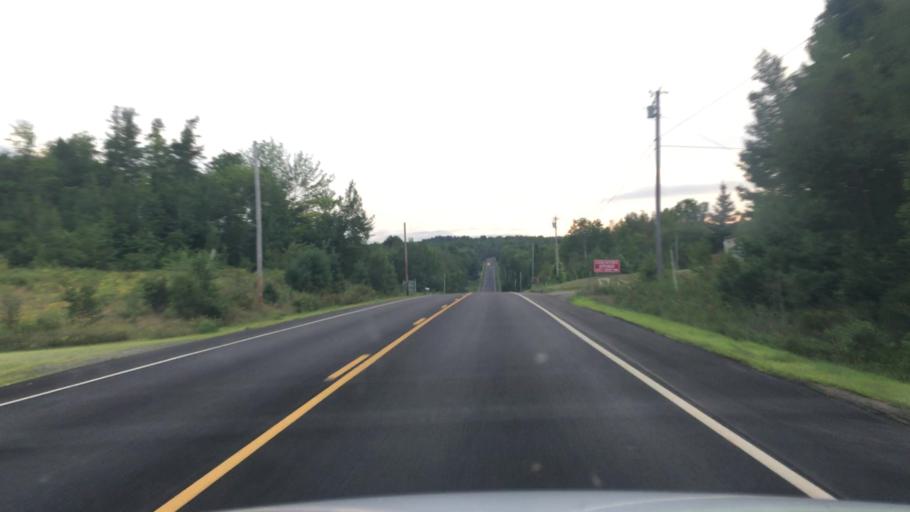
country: US
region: Maine
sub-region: Waldo County
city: Searsmont
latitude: 44.4043
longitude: -69.2306
